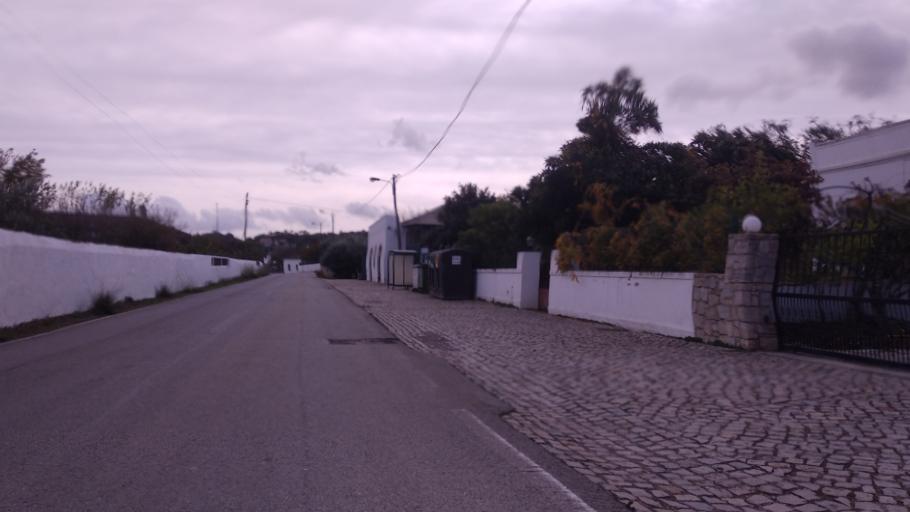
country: PT
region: Faro
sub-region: Sao Bras de Alportel
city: Sao Bras de Alportel
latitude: 37.1715
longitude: -7.9084
